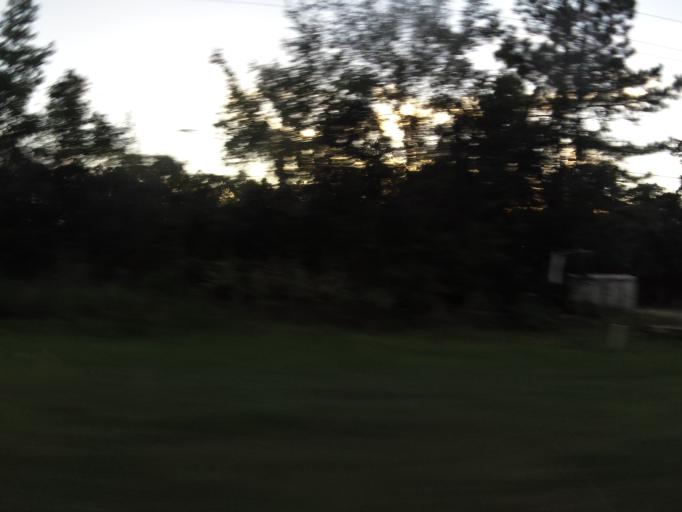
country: US
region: Georgia
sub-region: Camden County
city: Kingsland
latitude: 30.8277
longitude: -81.6958
